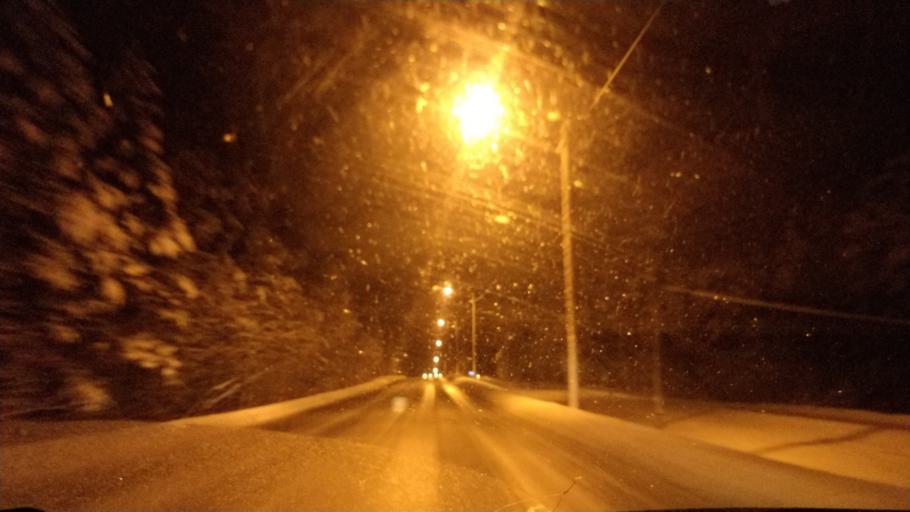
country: FI
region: Lapland
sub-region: Rovaniemi
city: Rovaniemi
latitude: 66.3213
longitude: 25.3580
